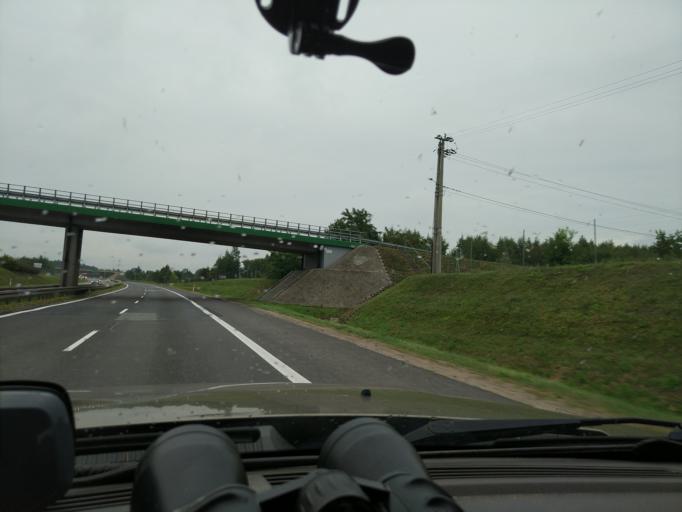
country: PL
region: Masovian Voivodeship
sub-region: Powiat ostrowski
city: Ostrow Mazowiecka
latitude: 52.8062
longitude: 21.8750
